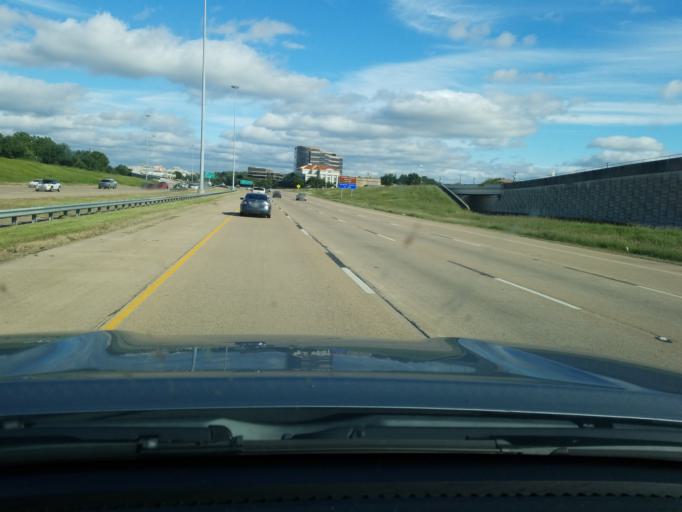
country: US
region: Texas
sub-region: Tarrant County
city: Westworth
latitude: 32.7326
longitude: -97.3692
